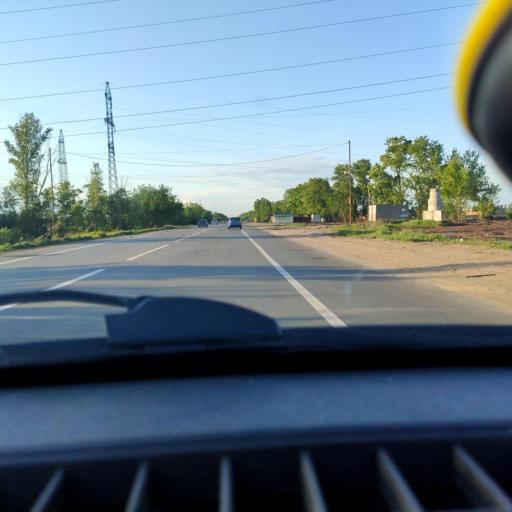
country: RU
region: Samara
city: Tol'yatti
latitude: 53.5806
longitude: 49.4035
